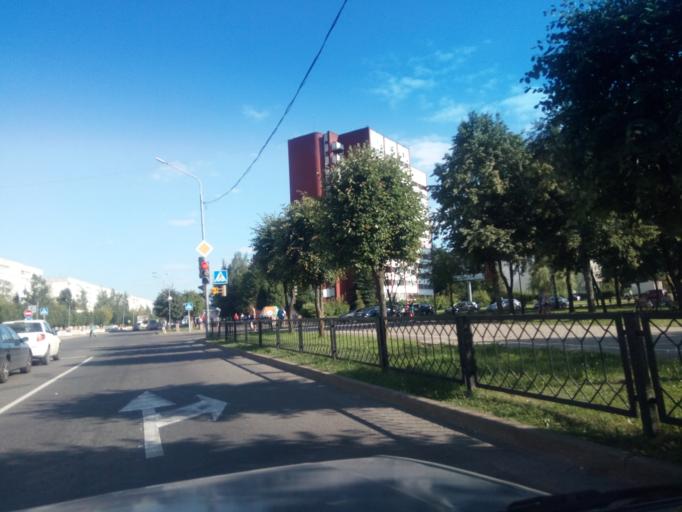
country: BY
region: Vitebsk
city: Navapolatsk
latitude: 55.5276
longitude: 28.6697
